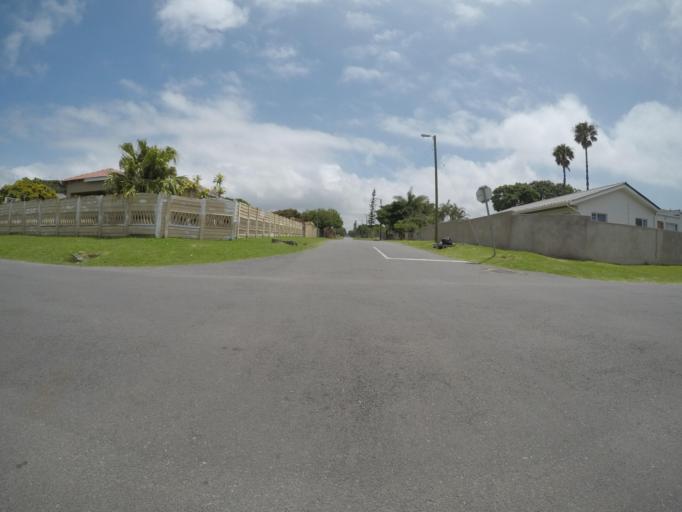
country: ZA
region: Eastern Cape
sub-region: Buffalo City Metropolitan Municipality
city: East London
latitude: -32.9445
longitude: 28.0137
